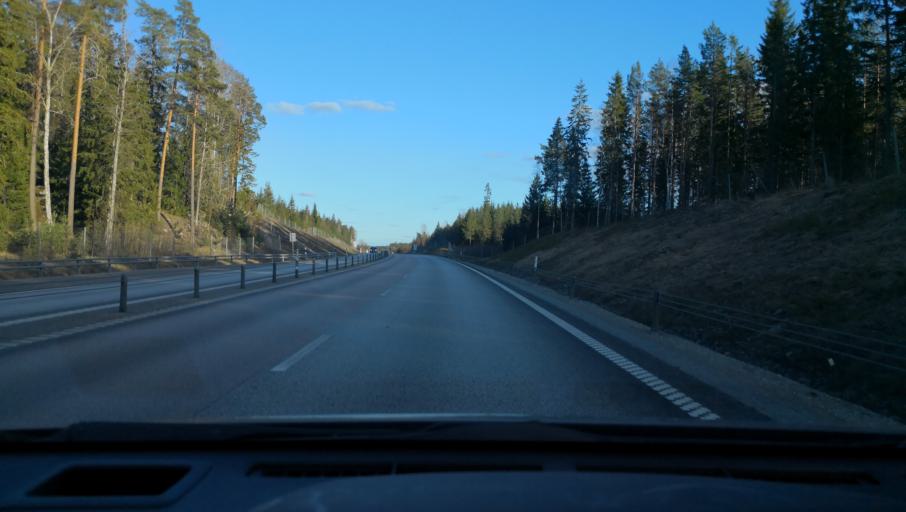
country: SE
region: Vaestmanland
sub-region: Sala Kommun
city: Sala
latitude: 59.9571
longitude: 16.4760
